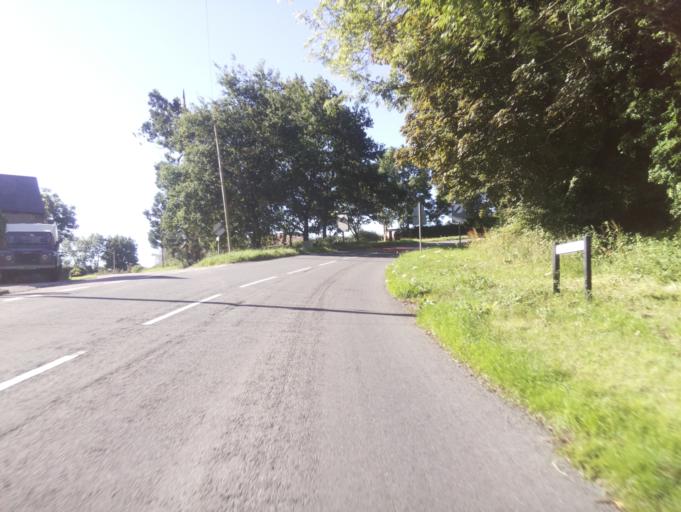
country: GB
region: England
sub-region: Gloucestershire
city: Coleford
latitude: 51.8290
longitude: -2.6113
